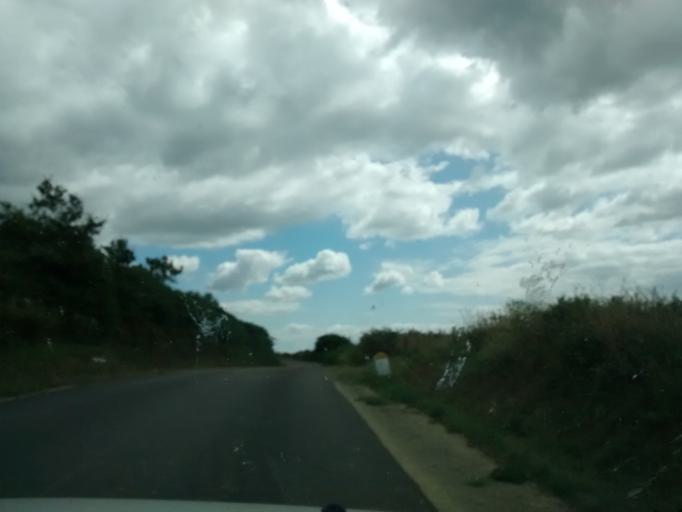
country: FR
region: Brittany
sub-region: Departement du Finistere
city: Plouider
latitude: 48.5925
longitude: -4.2890
